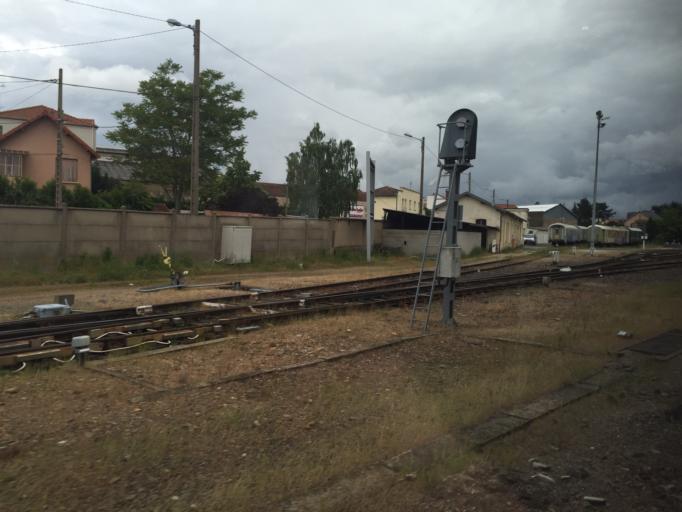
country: FR
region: Rhone-Alpes
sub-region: Departement de la Loire
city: Riorges
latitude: 46.0436
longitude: 4.0609
